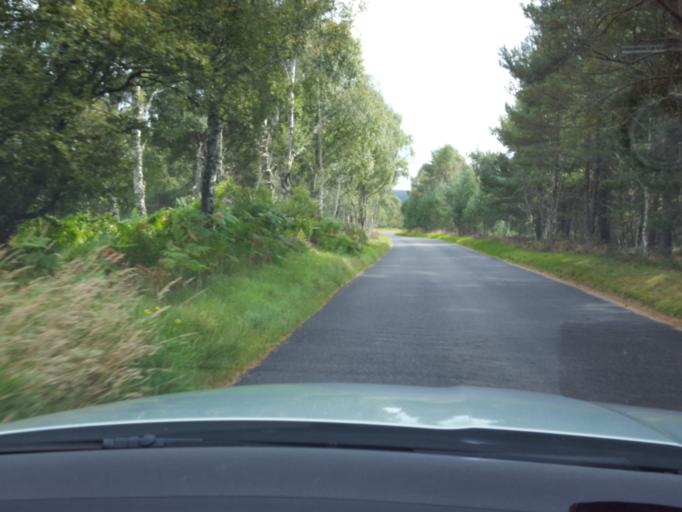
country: GB
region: Scotland
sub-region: Aberdeenshire
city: Ballater
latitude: 57.0819
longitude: -2.9406
